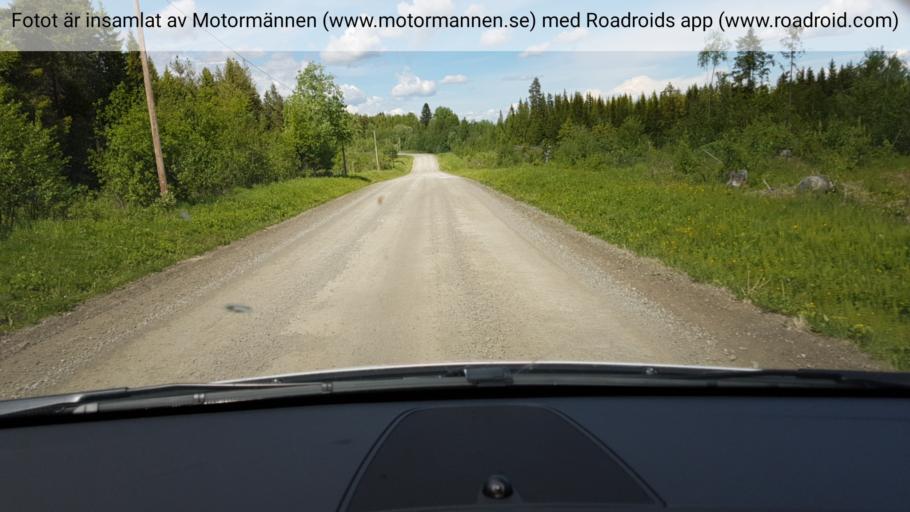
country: SE
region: Jaemtland
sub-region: Bergs Kommun
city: Hoverberg
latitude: 62.9759
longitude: 14.2179
